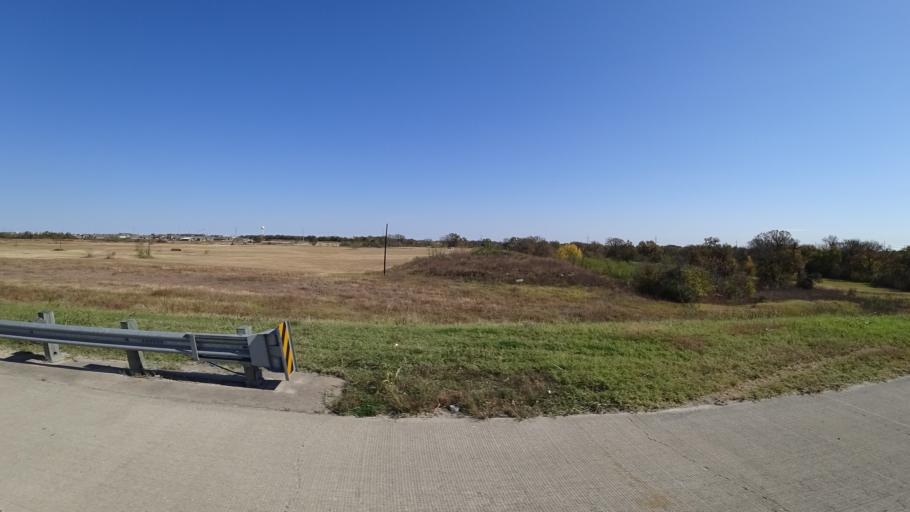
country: US
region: Texas
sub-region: Williamson County
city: Hutto
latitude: 30.5273
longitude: -97.5756
